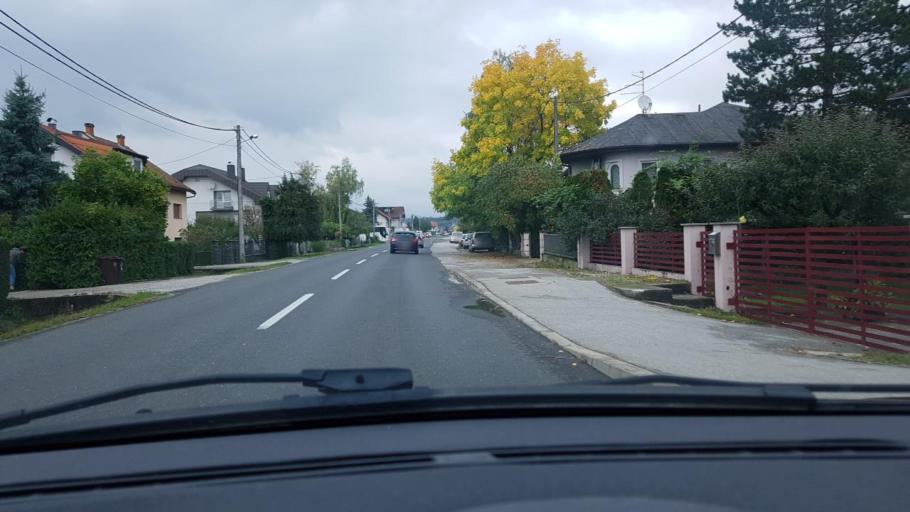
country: HR
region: Grad Zagreb
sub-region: Sesvete
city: Sesvete
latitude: 45.8473
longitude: 16.1103
